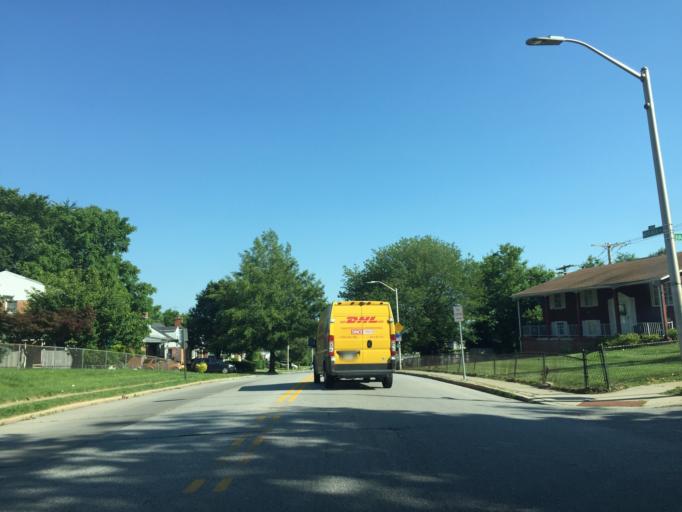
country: US
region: Maryland
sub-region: Baltimore County
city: Parkville
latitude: 39.3374
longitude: -76.5652
